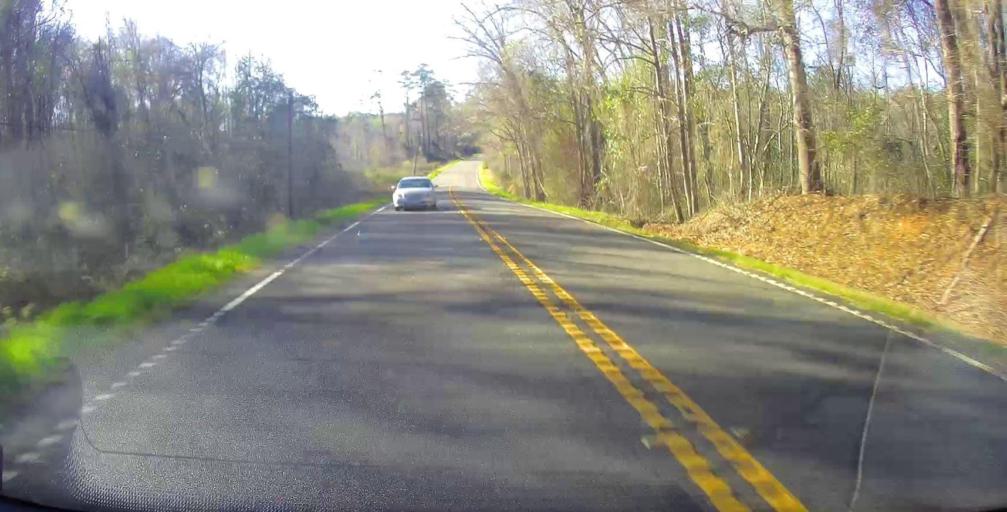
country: US
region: Georgia
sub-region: Macon County
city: Marshallville
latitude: 32.4480
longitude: -83.9061
